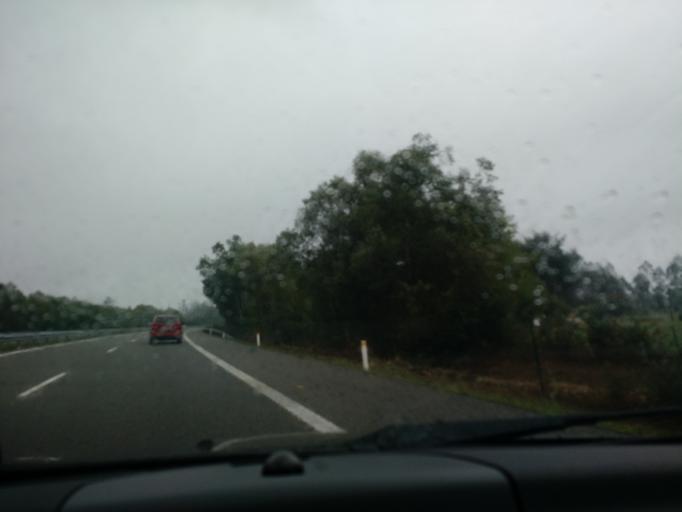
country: ES
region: Galicia
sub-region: Provincia da Coruna
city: Mesia
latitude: 43.1445
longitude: -8.3300
